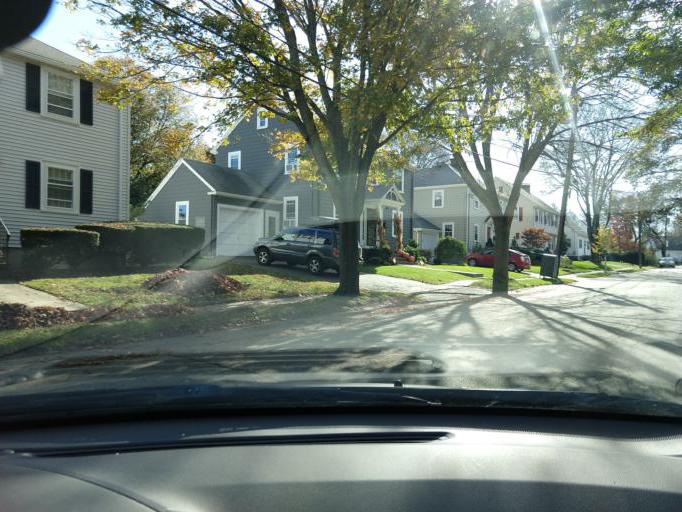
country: US
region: Massachusetts
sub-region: Middlesex County
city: Belmont
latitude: 42.3975
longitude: -71.1686
